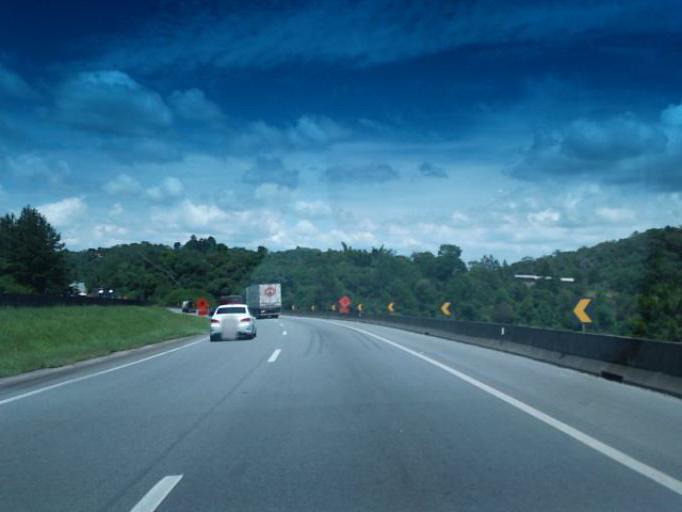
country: BR
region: Sao Paulo
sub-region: Juquitiba
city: Juquitiba
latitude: -23.9352
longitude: -47.0742
